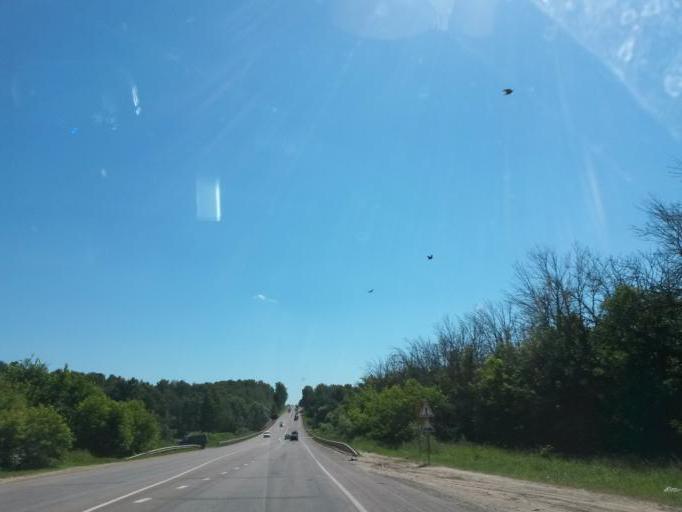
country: RU
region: Moskovskaya
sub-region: Chekhovskiy Rayon
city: Chekhov
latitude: 55.1120
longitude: 37.4473
